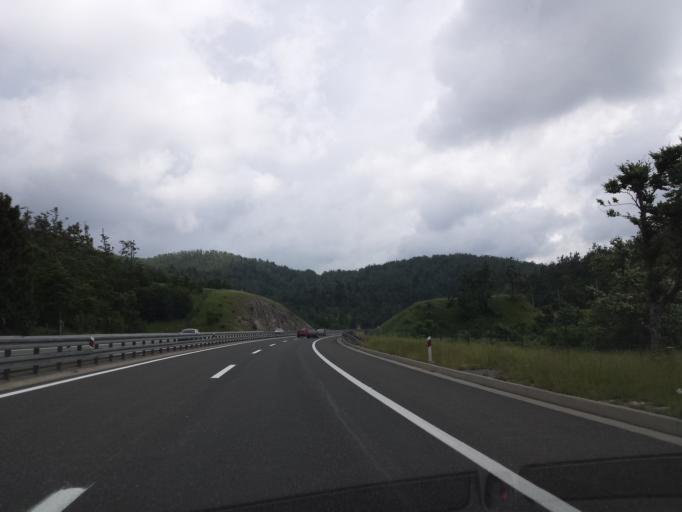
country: HR
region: Primorsko-Goranska
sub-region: Grad Delnice
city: Delnice
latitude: 45.3356
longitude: 14.7392
